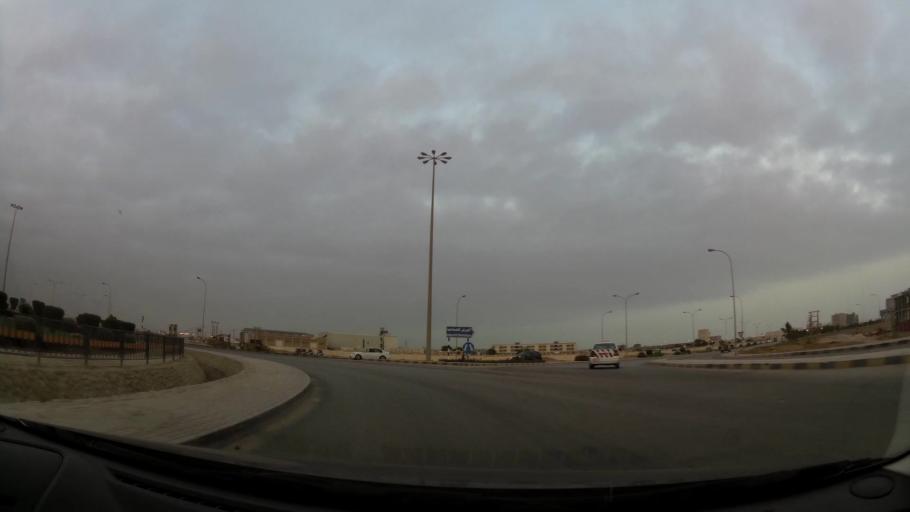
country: OM
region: Zufar
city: Salalah
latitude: 17.0309
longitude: 54.0293
